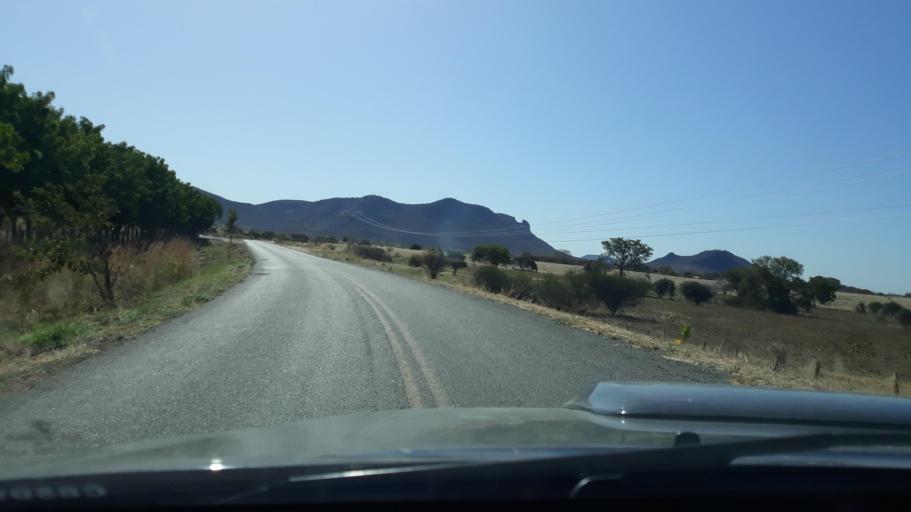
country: BR
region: Bahia
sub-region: Guanambi
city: Guanambi
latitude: -14.1627
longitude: -42.8150
